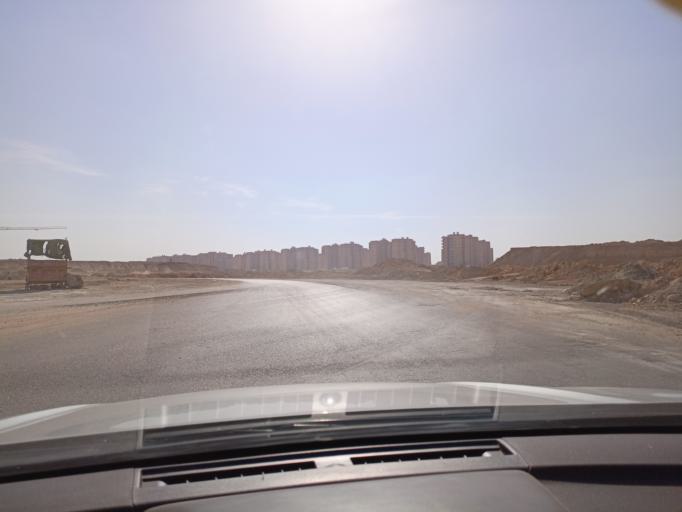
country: EG
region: Muhafazat al Qalyubiyah
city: Al Khankah
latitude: 30.0334
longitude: 31.6808
